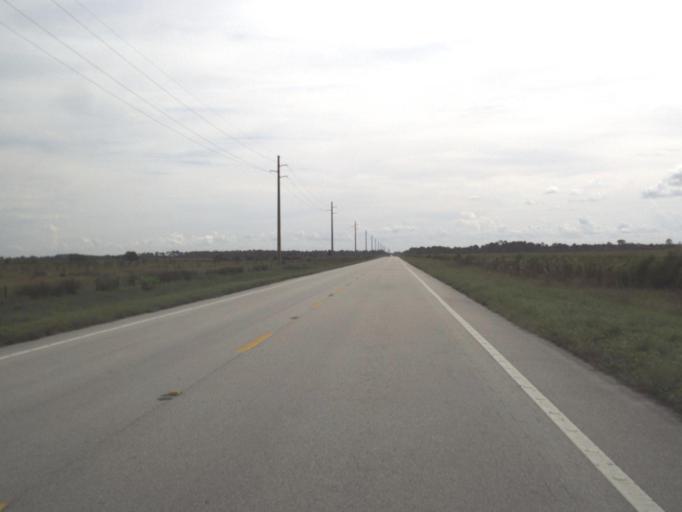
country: US
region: Florida
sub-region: Highlands County
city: Placid Lakes
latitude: 27.2090
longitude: -81.5233
